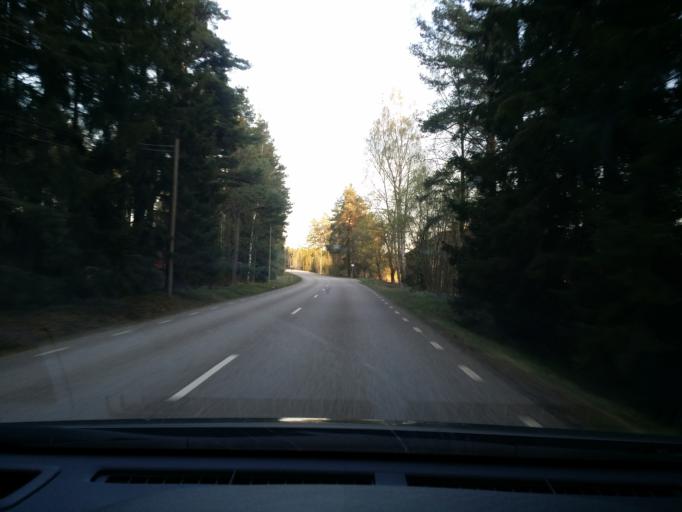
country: SE
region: Vaestmanland
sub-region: Sala Kommun
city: Sala
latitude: 59.8338
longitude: 16.5060
